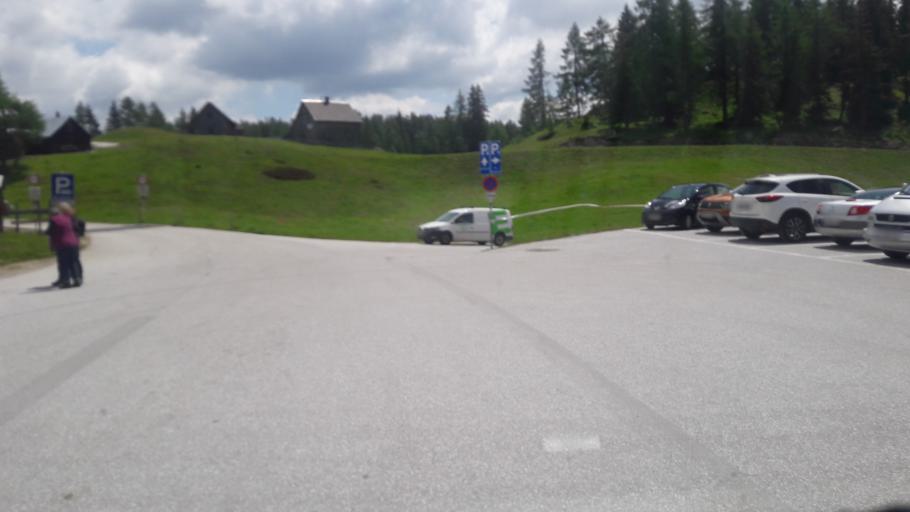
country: AT
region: Styria
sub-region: Politischer Bezirk Liezen
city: Tauplitz
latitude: 47.5933
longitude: 13.9859
